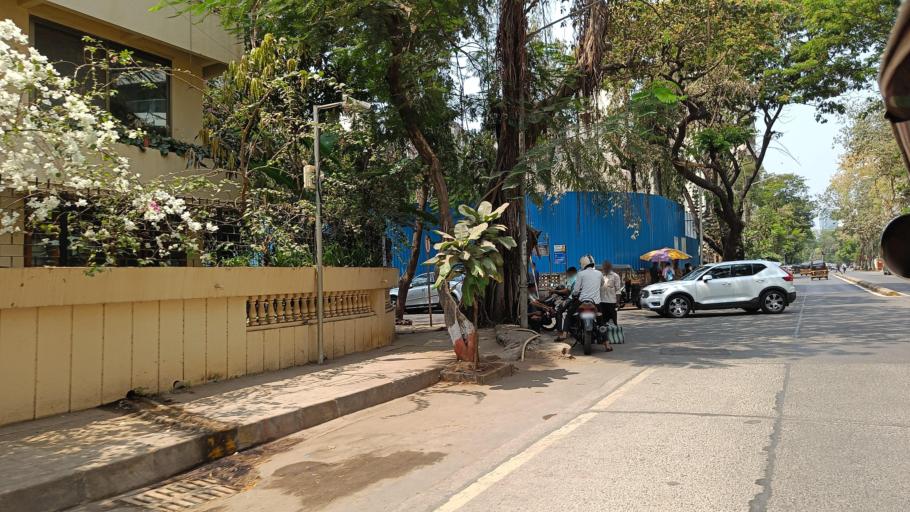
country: IN
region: Maharashtra
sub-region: Mumbai Suburban
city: Mumbai
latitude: 19.1071
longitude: 72.8318
